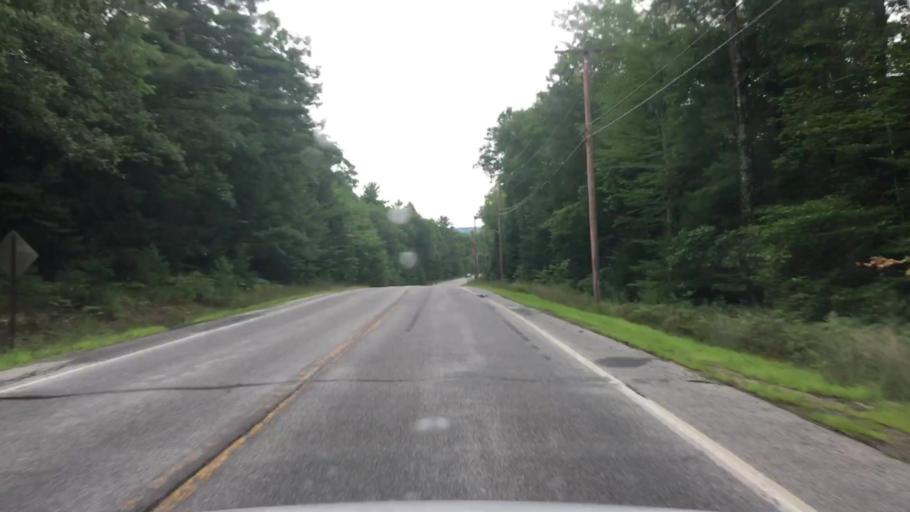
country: US
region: Maine
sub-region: York County
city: Cornish
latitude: 43.8161
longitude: -70.7765
